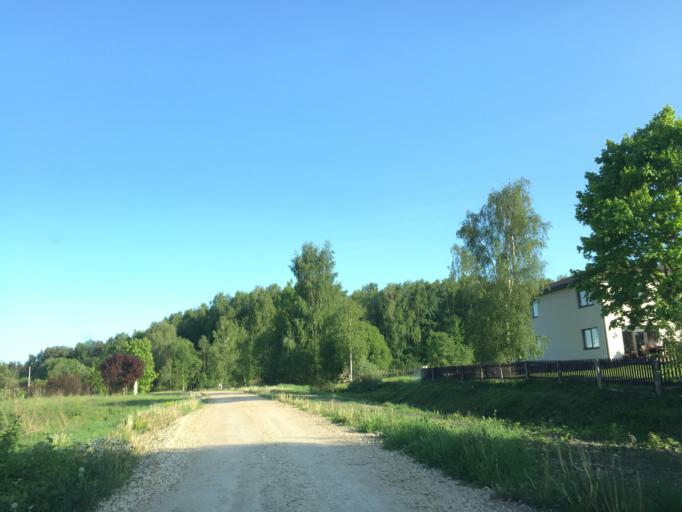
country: LV
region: Kekava
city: Kekava
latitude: 56.8219
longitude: 24.2584
